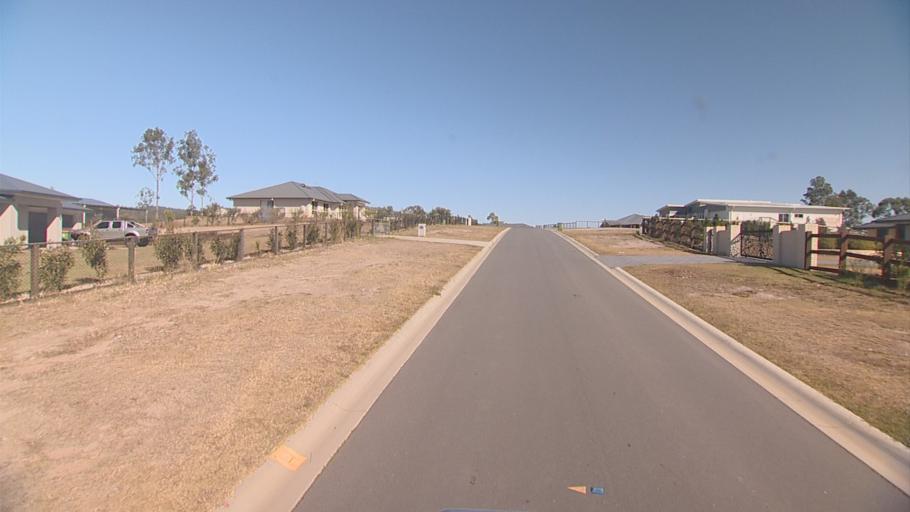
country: AU
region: Queensland
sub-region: Logan
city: Cedar Vale
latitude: -27.8662
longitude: 153.0487
